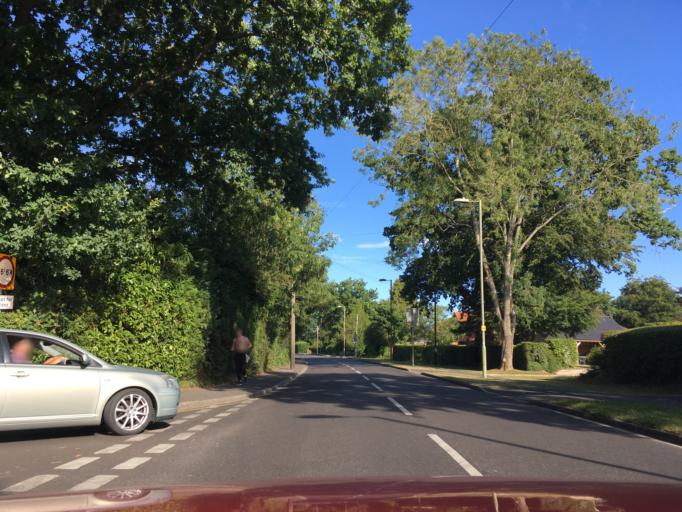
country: GB
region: England
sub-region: Hampshire
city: Romsey
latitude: 50.9871
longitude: -1.4712
